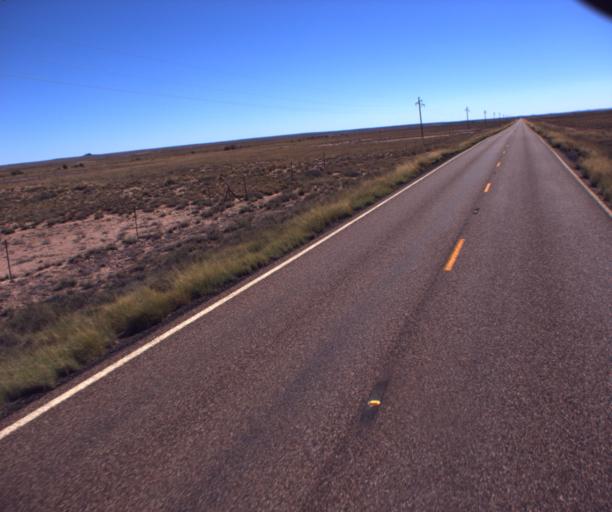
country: US
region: Arizona
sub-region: Navajo County
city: Holbrook
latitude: 35.1253
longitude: -110.0921
